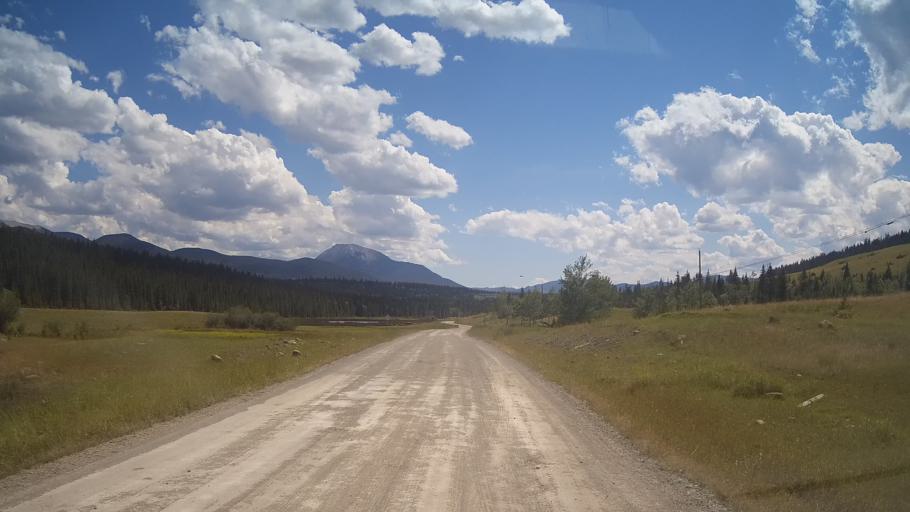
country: CA
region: British Columbia
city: Lillooet
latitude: 51.3018
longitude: -121.9834
